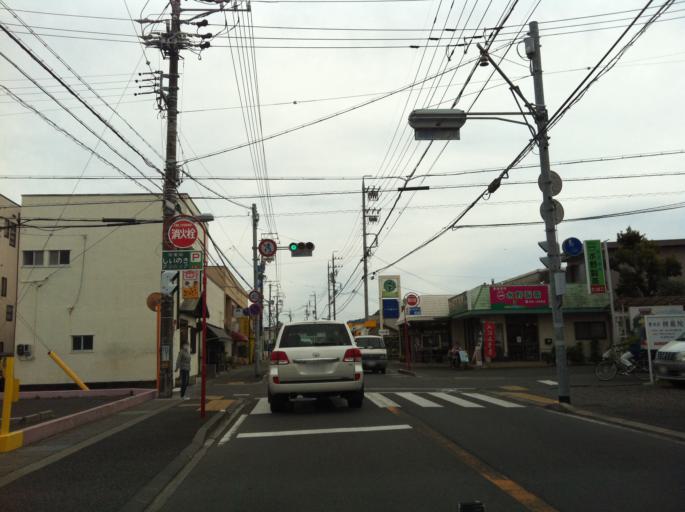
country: JP
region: Shizuoka
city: Shizuoka-shi
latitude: 35.0059
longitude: 138.4655
